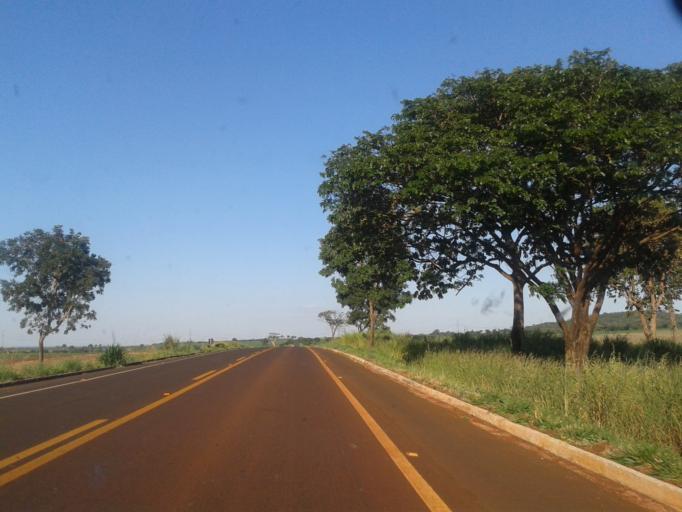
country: BR
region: Minas Gerais
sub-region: Capinopolis
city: Capinopolis
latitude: -18.7121
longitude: -49.8051
